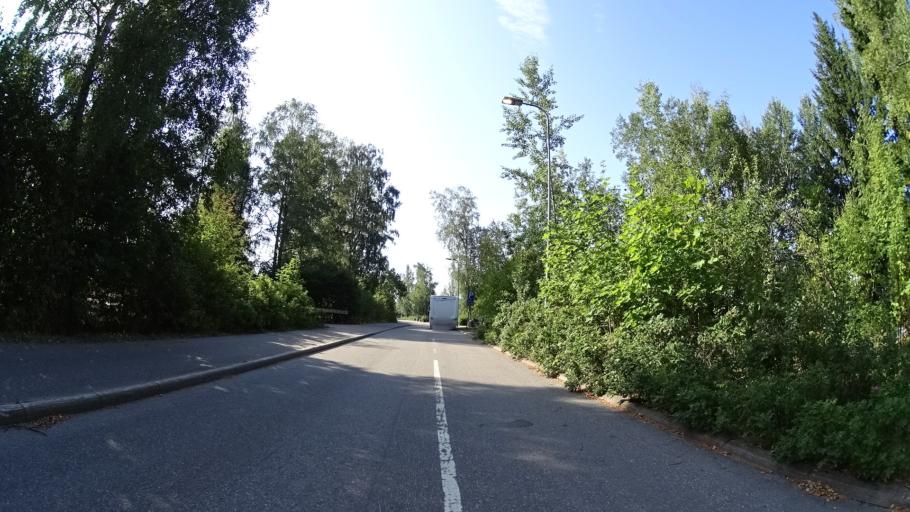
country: FI
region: Uusimaa
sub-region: Helsinki
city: Otaniemi
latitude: 60.1926
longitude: 24.8043
